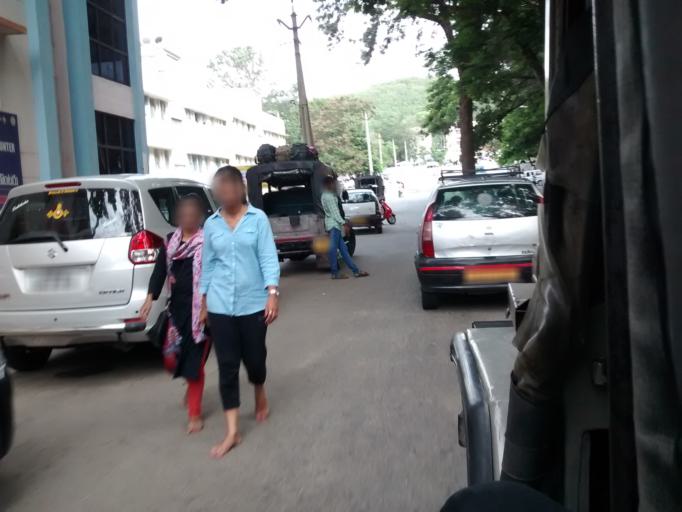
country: IN
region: Andhra Pradesh
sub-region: Chittoor
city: Tirumala
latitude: 13.6799
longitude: 79.3529
